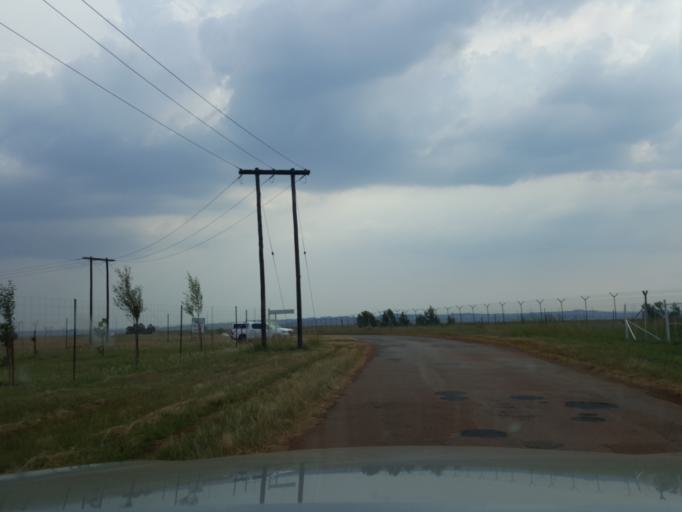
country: ZA
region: Gauteng
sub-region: City of Tshwane Metropolitan Municipality
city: Centurion
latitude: -25.8767
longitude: 28.3264
